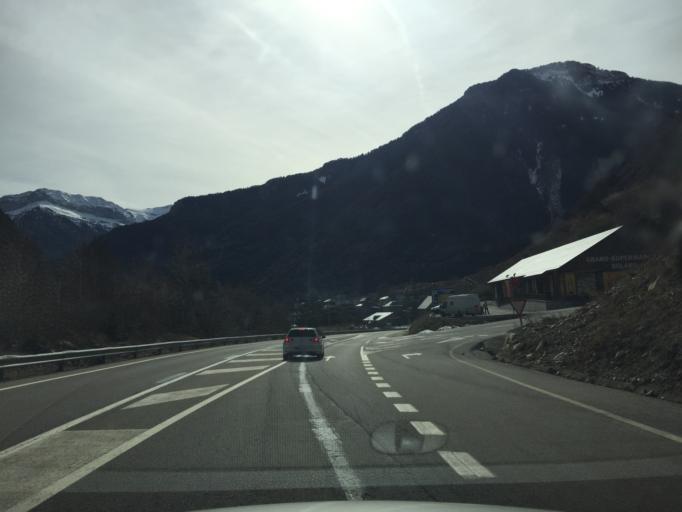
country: ES
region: Aragon
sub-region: Provincia de Huesca
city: Bielsa
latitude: 42.6655
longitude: 0.2122
